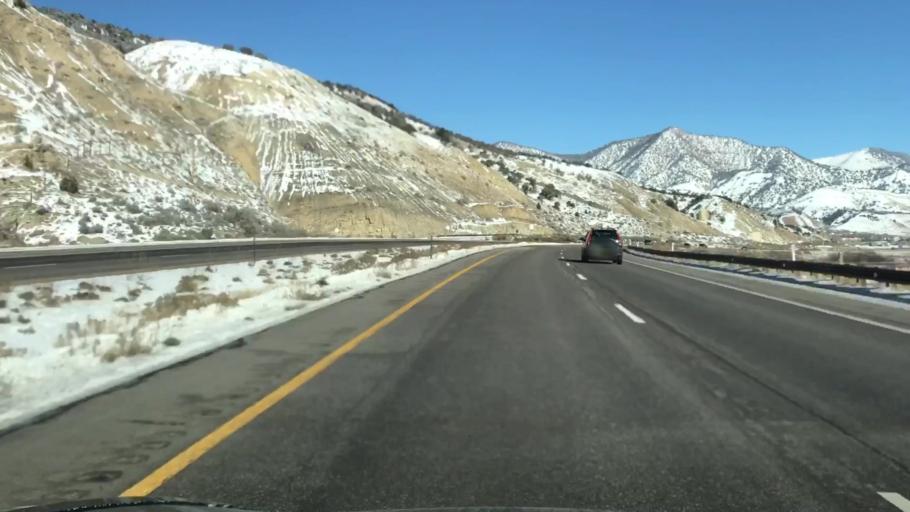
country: US
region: Colorado
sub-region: Eagle County
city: Gypsum
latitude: 39.6437
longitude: -107.0802
